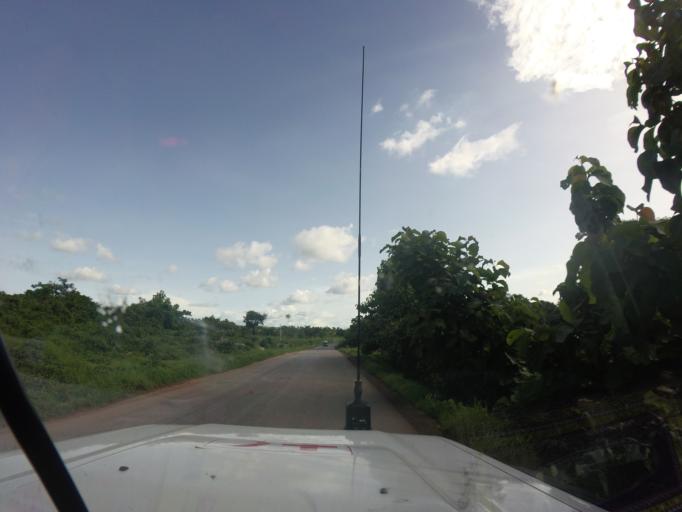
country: GN
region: Kindia
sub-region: Kindia
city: Kindia
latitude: 10.1128
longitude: -12.5477
